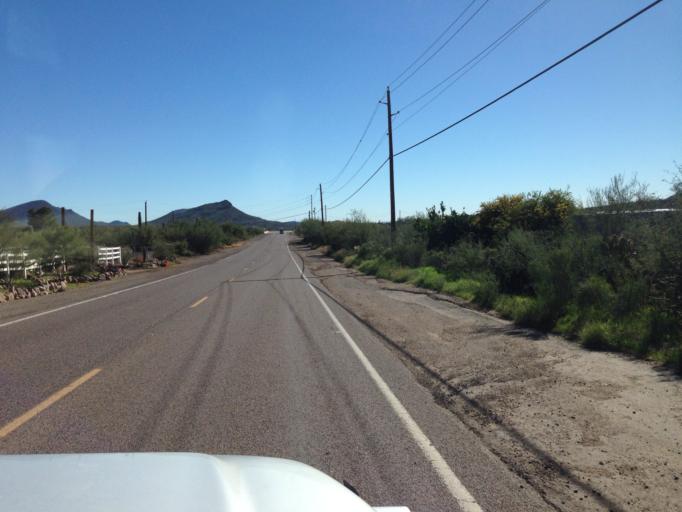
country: US
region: Arizona
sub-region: Maricopa County
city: New River
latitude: 33.9111
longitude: -112.0862
